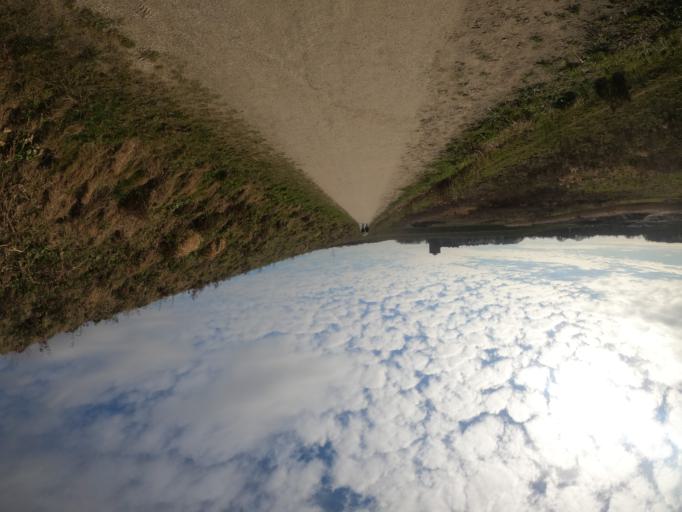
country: NL
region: Gelderland
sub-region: Gemeente Ermelo
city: Horst
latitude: 52.3271
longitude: 5.5807
